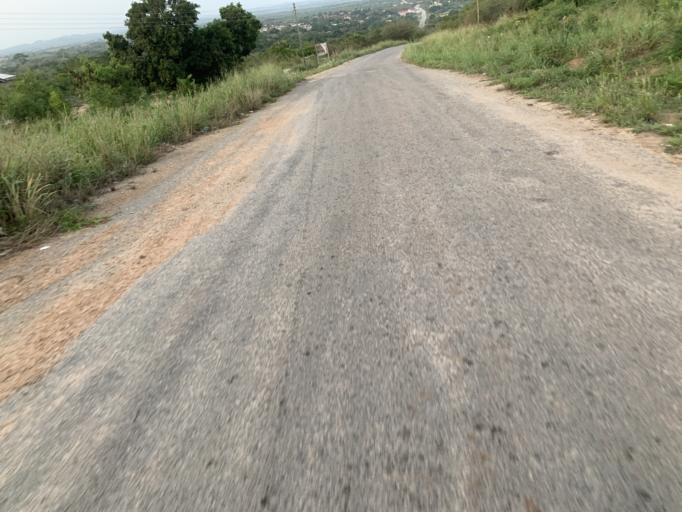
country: GH
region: Central
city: Winneba
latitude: 5.3682
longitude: -0.6182
